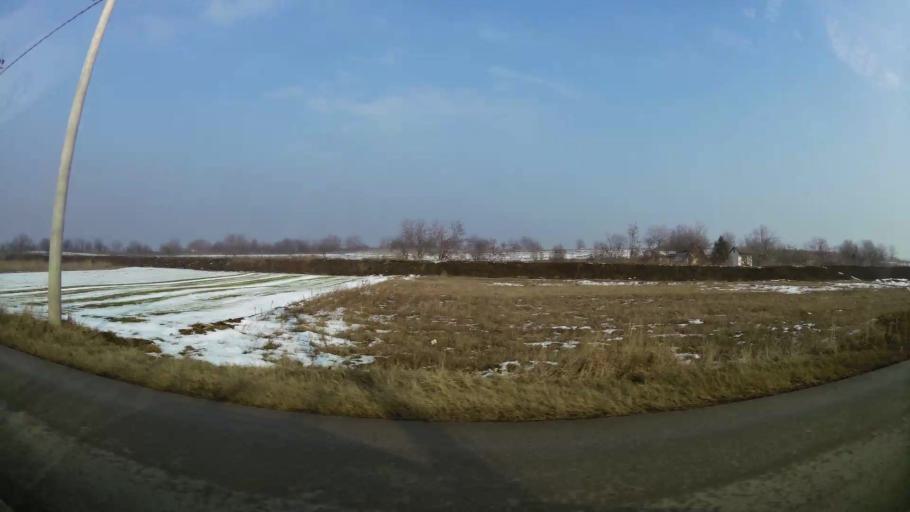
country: MK
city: Kadino
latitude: 41.9745
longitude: 21.6038
